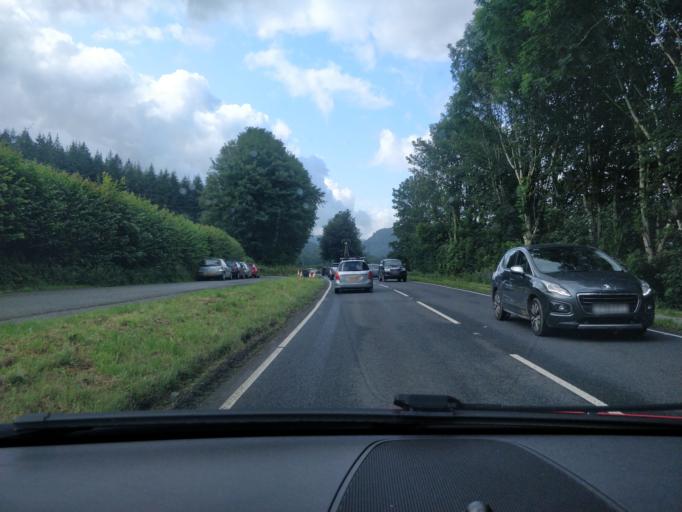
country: GB
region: Wales
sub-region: Conwy
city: Betws-y-Coed
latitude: 53.1048
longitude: -3.7864
